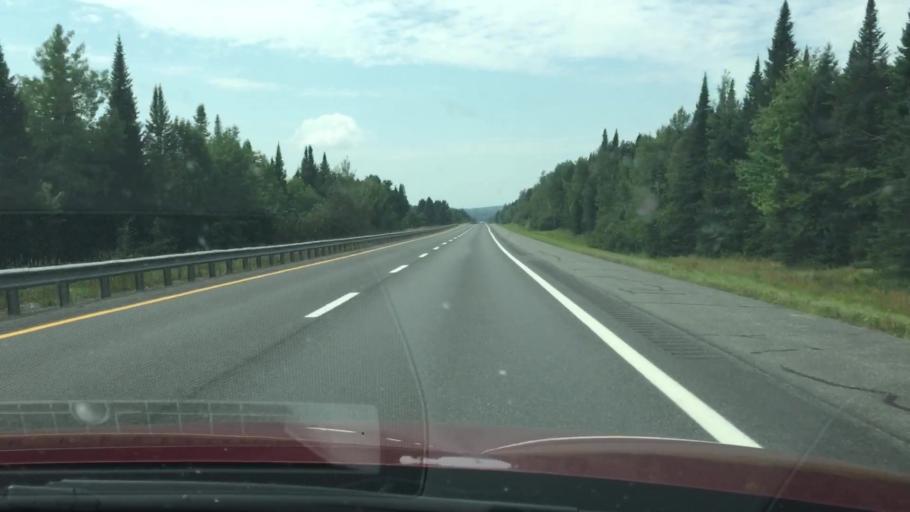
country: US
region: Maine
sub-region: Aroostook County
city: Hodgdon
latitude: 46.1188
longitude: -68.1241
